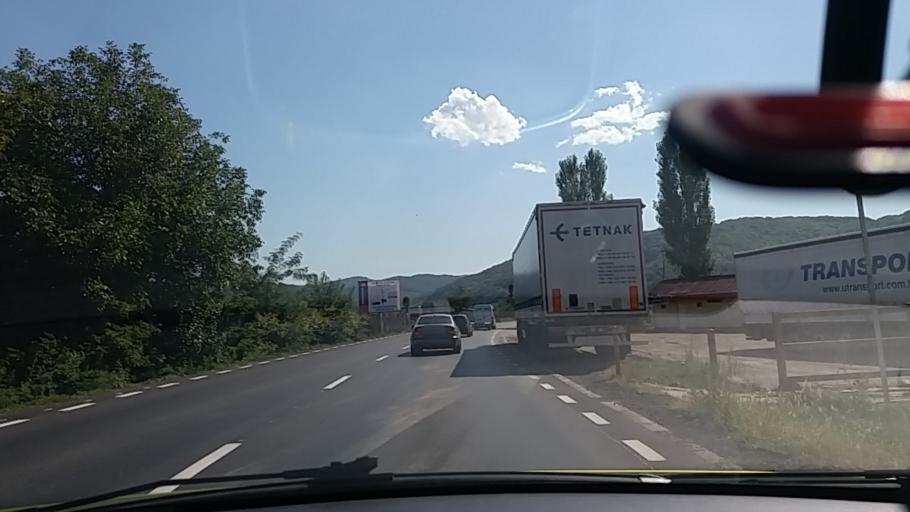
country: RO
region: Hunedoara
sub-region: Comuna Ilia
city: Ilia
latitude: 45.9311
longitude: 22.6567
